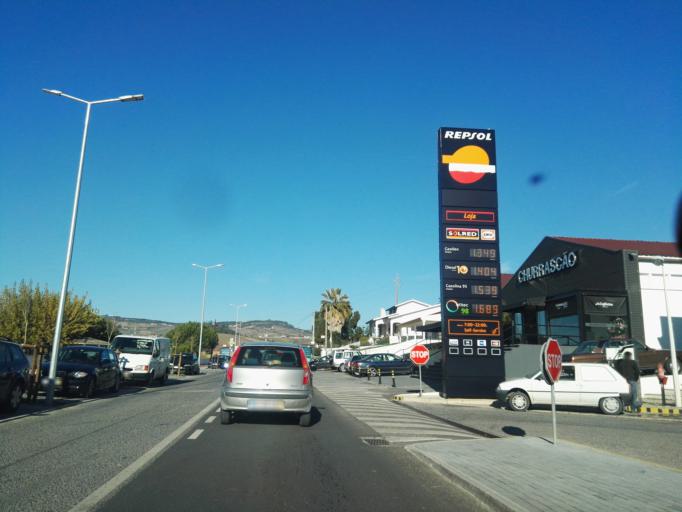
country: PT
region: Lisbon
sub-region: Arruda Dos Vinhos
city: Arruda dos Vinhos
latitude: 38.9885
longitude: -9.0765
